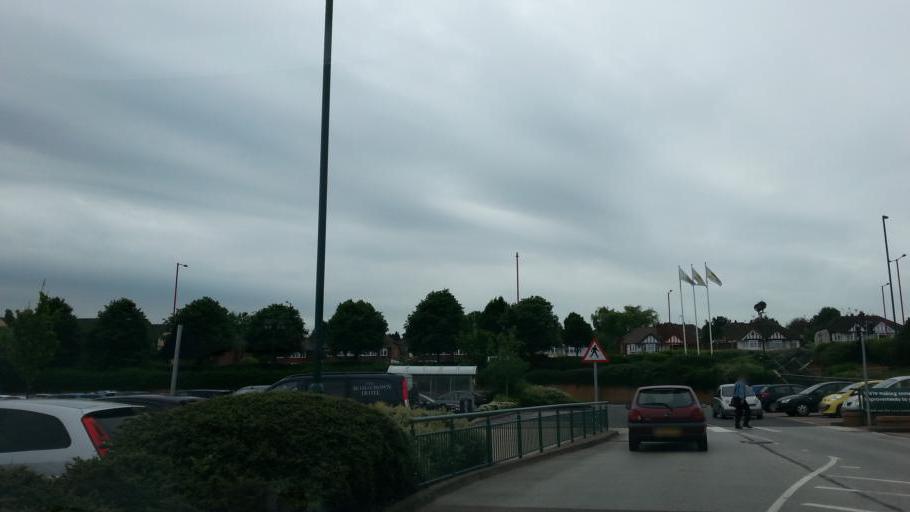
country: GB
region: England
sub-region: Worcestershire
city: Barnt Green
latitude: 52.3965
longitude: -2.0068
